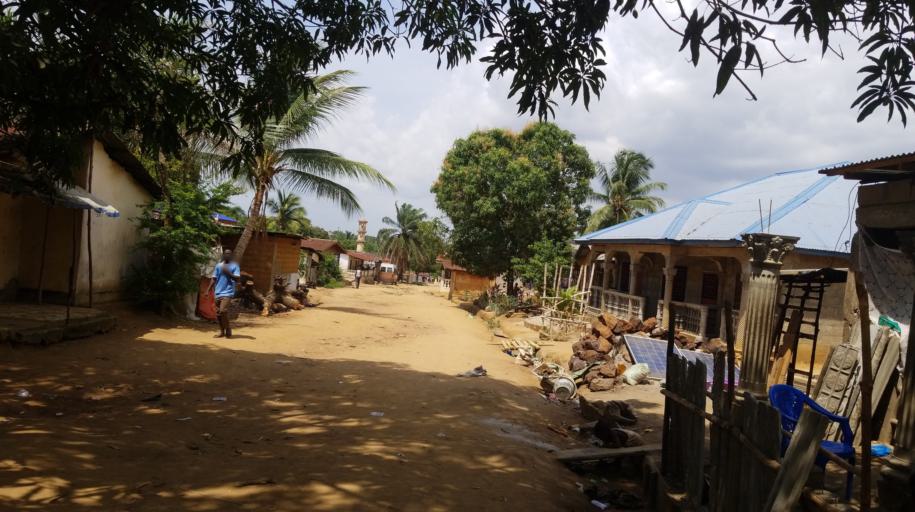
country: SL
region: Western Area
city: Waterloo
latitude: 8.3233
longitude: -13.0554
